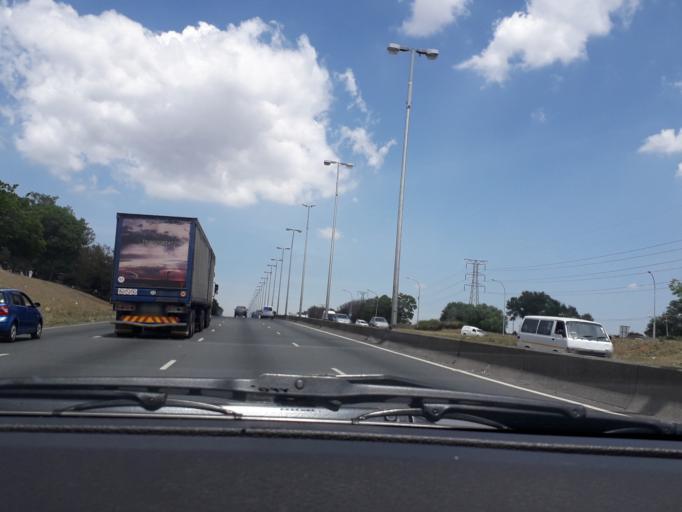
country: ZA
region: Gauteng
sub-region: City of Johannesburg Metropolitan Municipality
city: Johannesburg
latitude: -26.2447
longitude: 28.0062
